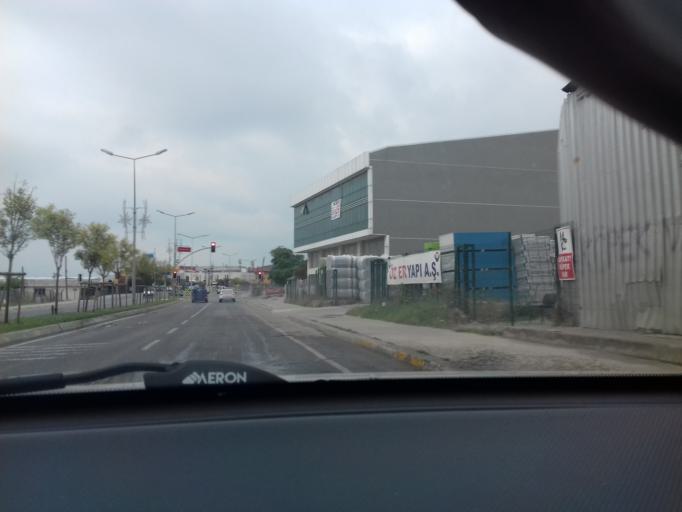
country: TR
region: Istanbul
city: Icmeler
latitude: 40.8933
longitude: 29.3546
